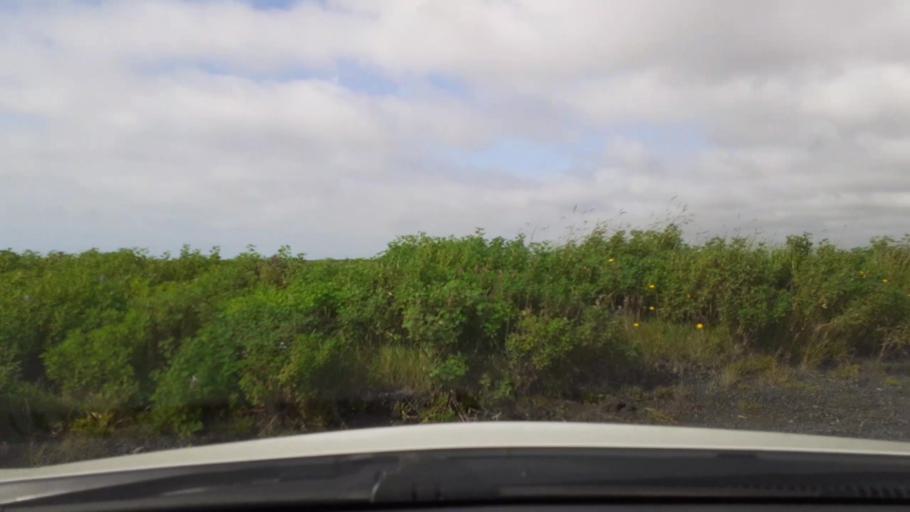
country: IS
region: South
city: THorlakshoefn
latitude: 63.8687
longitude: -21.3828
